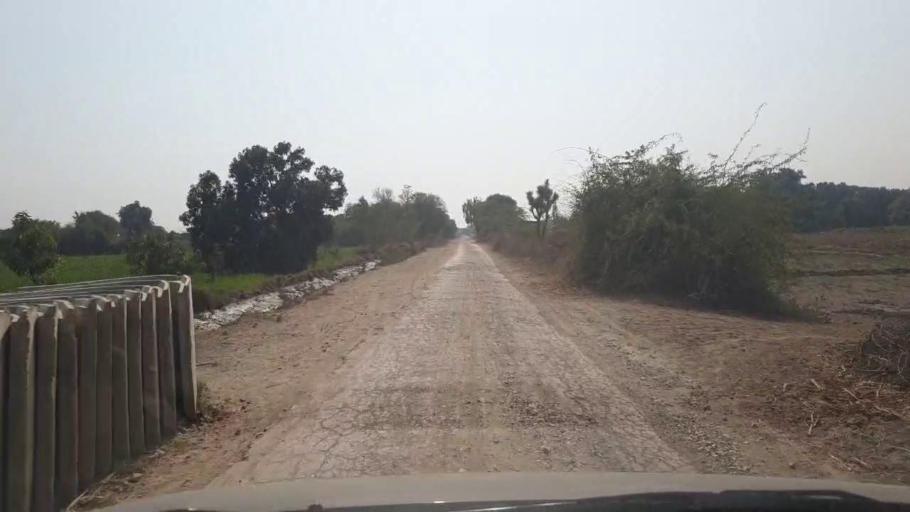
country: PK
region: Sindh
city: Digri
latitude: 25.2457
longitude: 69.1446
